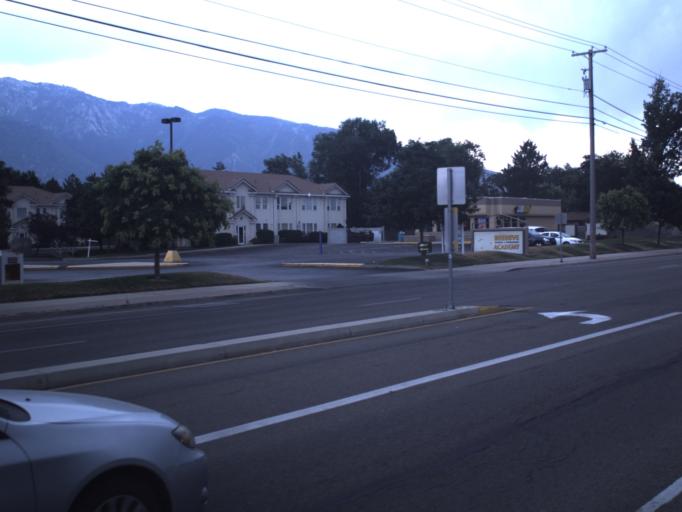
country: US
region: Utah
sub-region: Salt Lake County
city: White City
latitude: 40.5785
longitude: -111.8723
